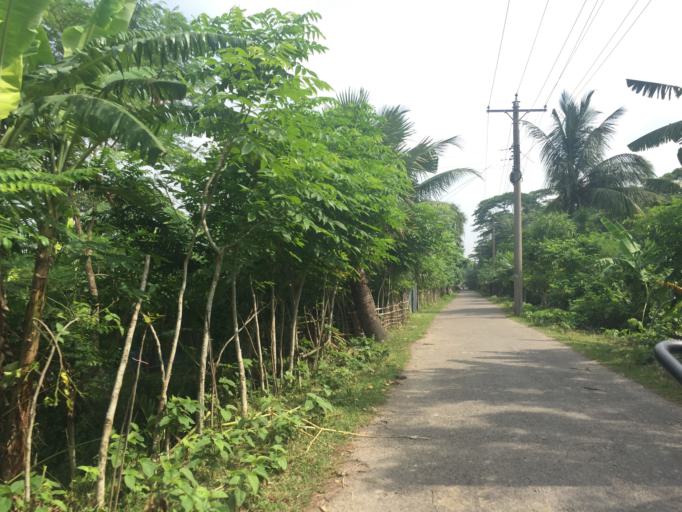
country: BD
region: Barisal
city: Mathba
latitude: 22.2362
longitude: 89.9153
